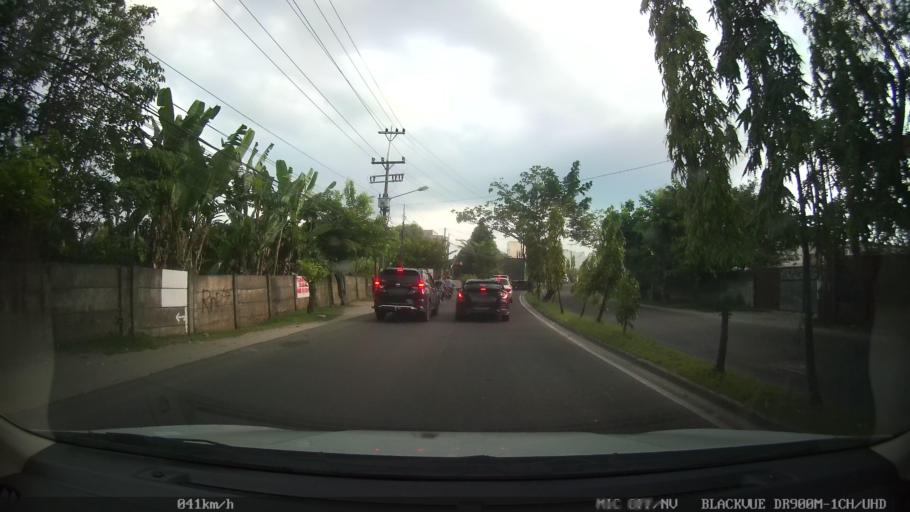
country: ID
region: North Sumatra
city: Sunggal
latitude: 3.5359
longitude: 98.6224
